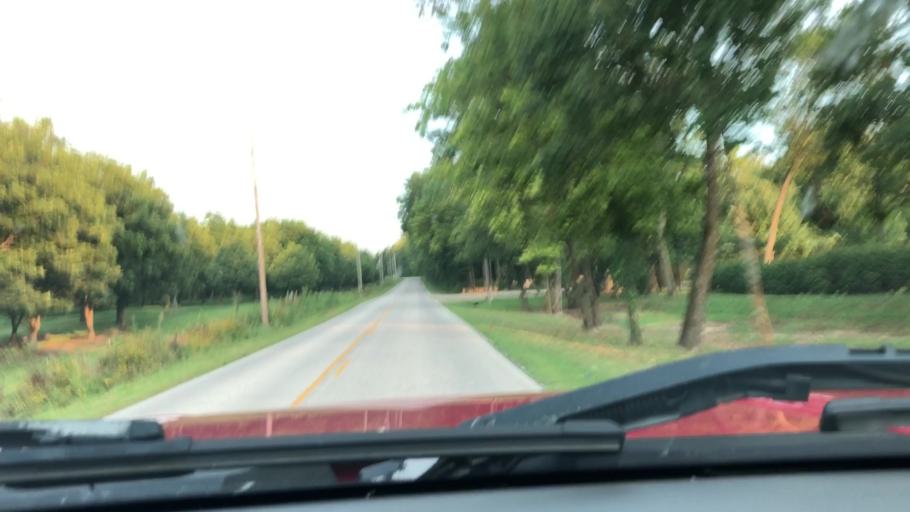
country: US
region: Missouri
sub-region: Jasper County
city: Joplin
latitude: 37.0198
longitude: -94.5094
